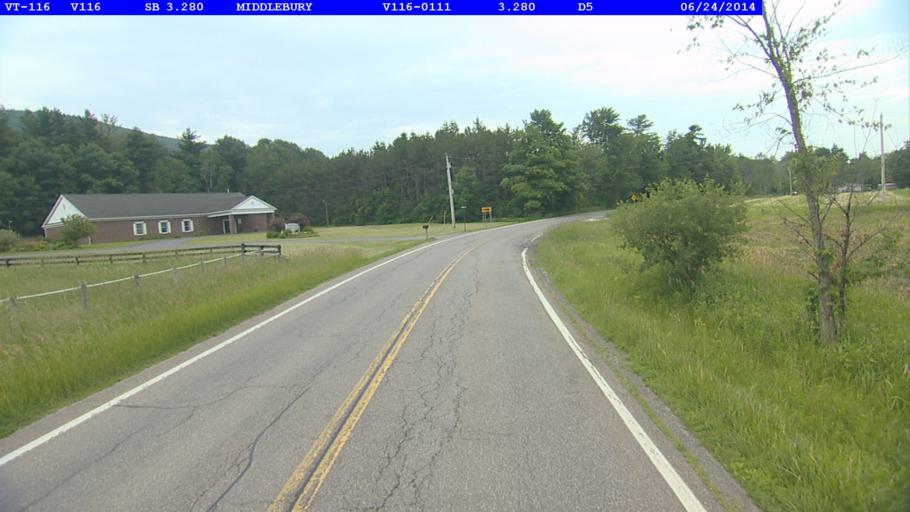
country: US
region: Vermont
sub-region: Addison County
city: Middlebury (village)
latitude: 44.0105
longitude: -73.0978
